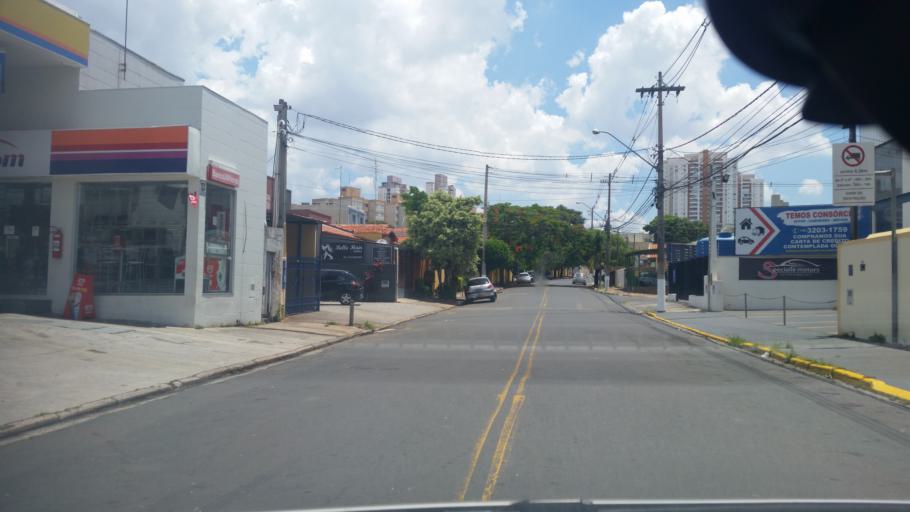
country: BR
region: Sao Paulo
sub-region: Campinas
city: Campinas
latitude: -22.8771
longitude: -47.0446
